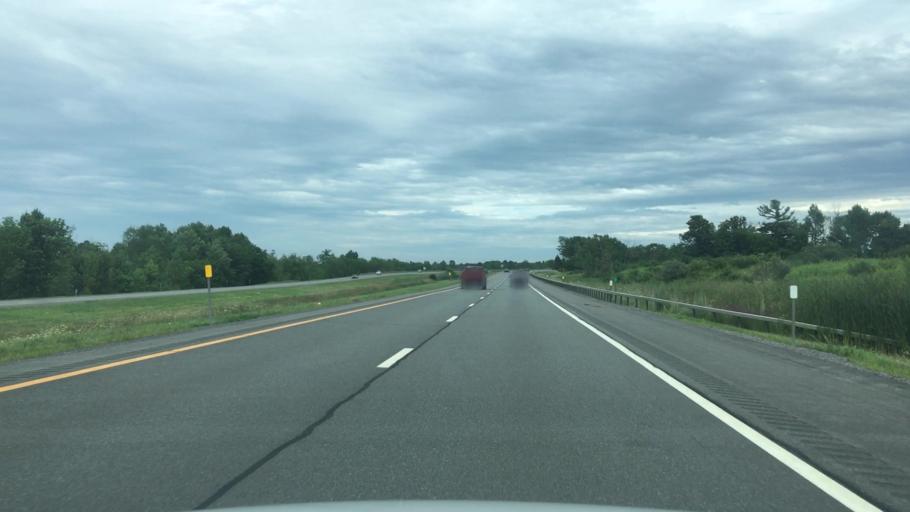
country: US
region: New York
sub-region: Schoharie County
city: Schoharie
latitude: 42.7205
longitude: -74.2487
